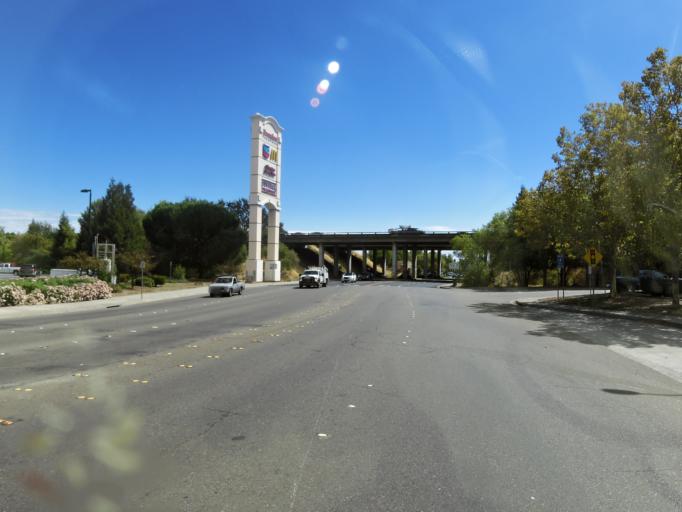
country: US
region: California
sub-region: Solano County
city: Vacaville
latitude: 38.3518
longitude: -121.9863
